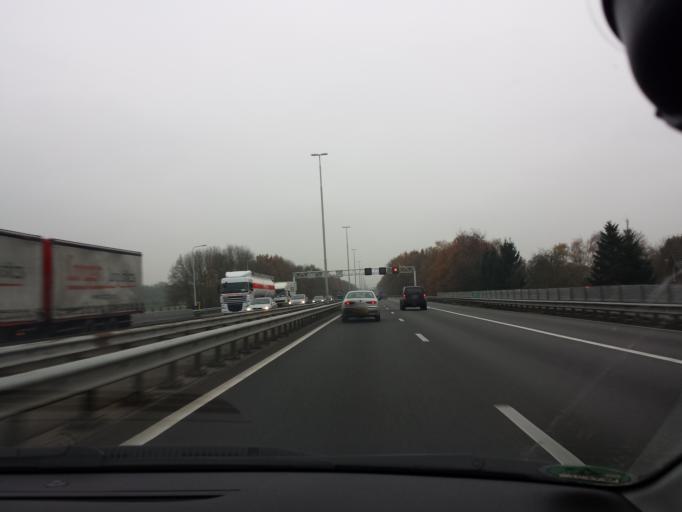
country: NL
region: Limburg
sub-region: Gemeente Sittard-Geleen
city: Born
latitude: 51.0267
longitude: 5.8177
